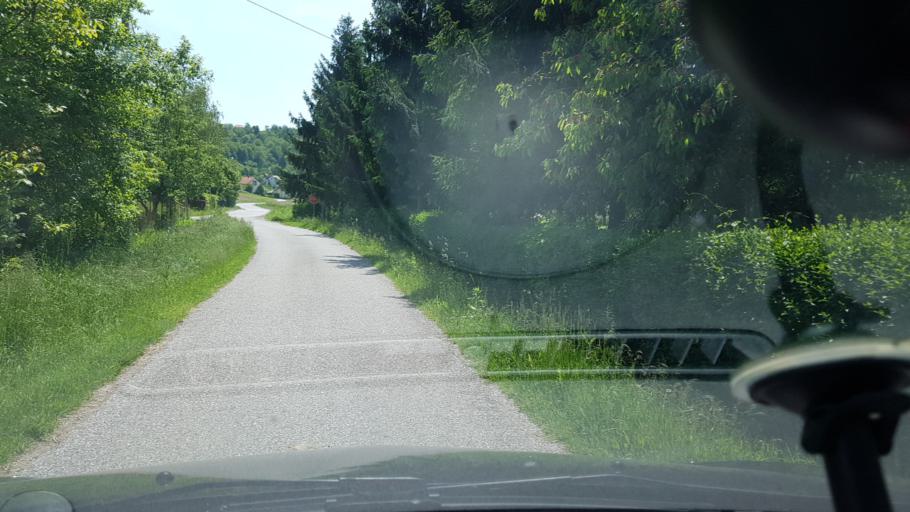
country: HR
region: Krapinsko-Zagorska
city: Marija Bistrica
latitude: 45.9347
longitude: 16.1902
